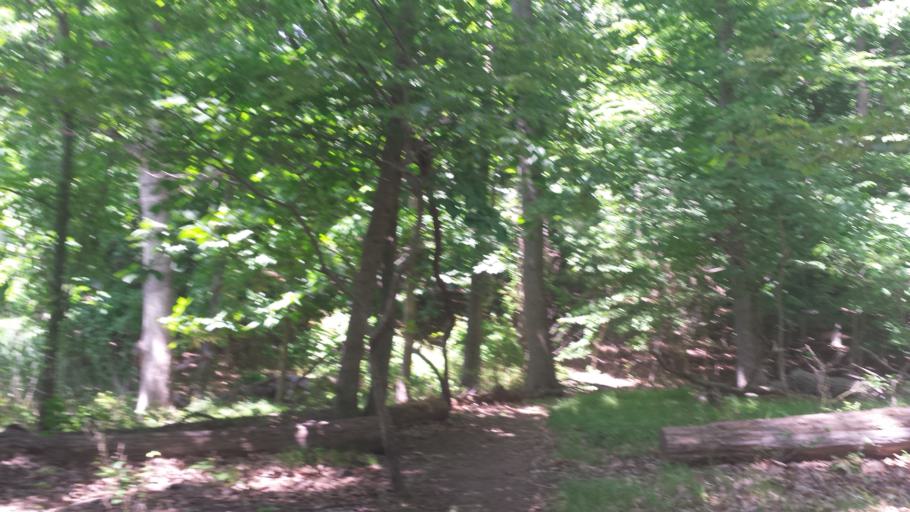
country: US
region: New York
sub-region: Westchester County
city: Harrison
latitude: 40.9529
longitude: -73.7000
